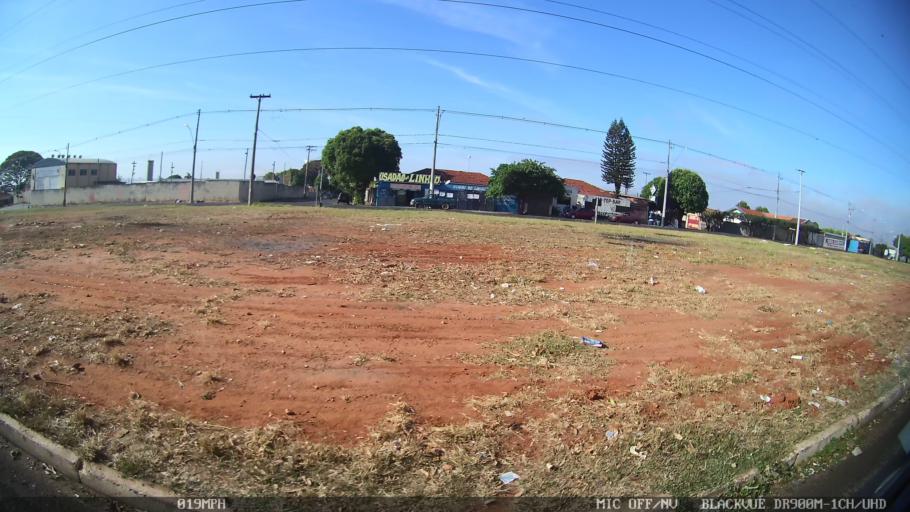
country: BR
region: Sao Paulo
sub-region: Sao Jose Do Rio Preto
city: Sao Jose do Rio Preto
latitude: -20.7806
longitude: -49.4053
